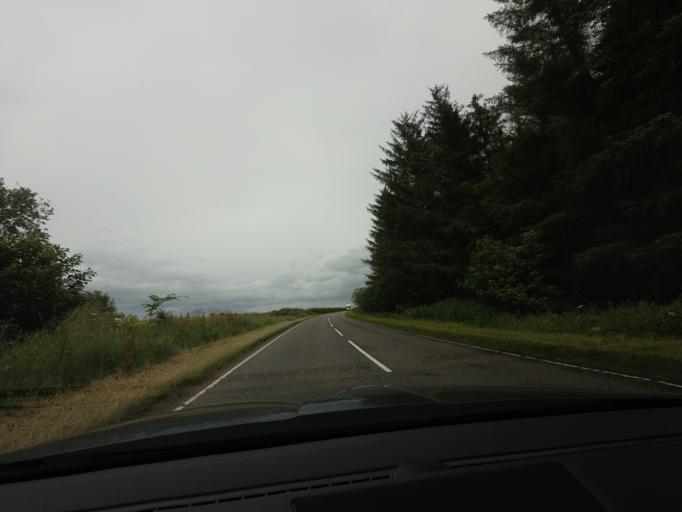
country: GB
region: Scotland
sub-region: Moray
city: Findochty
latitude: 57.6738
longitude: -2.9122
